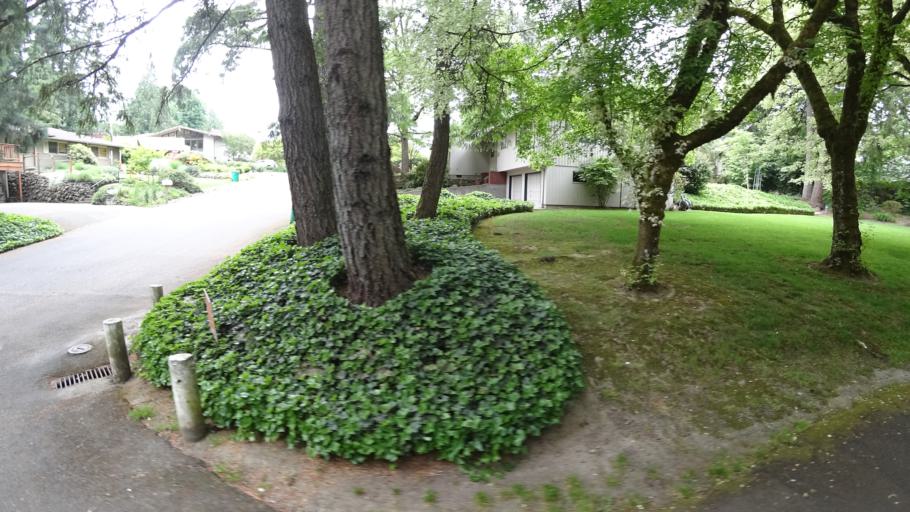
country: US
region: Oregon
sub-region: Washington County
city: Garden Home-Whitford
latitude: 45.4728
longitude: -122.7403
